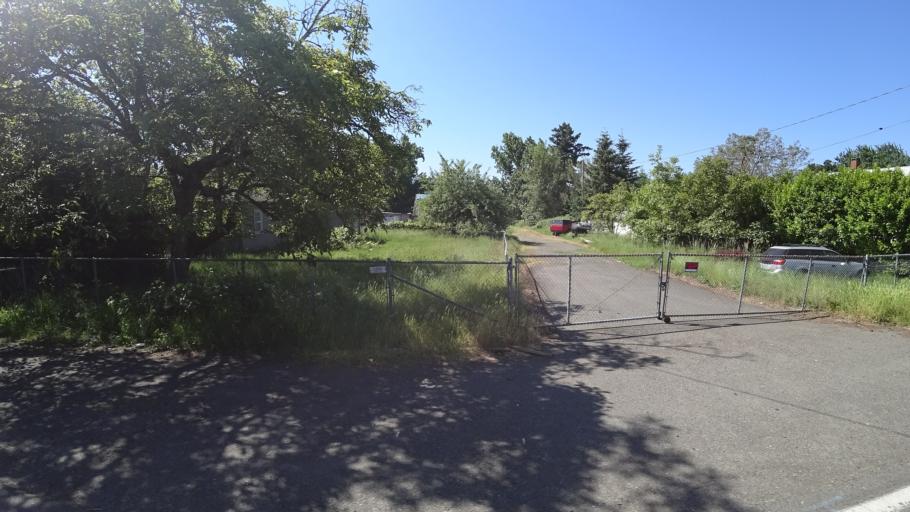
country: US
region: Oregon
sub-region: Multnomah County
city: Lents
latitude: 45.4827
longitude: -122.5532
